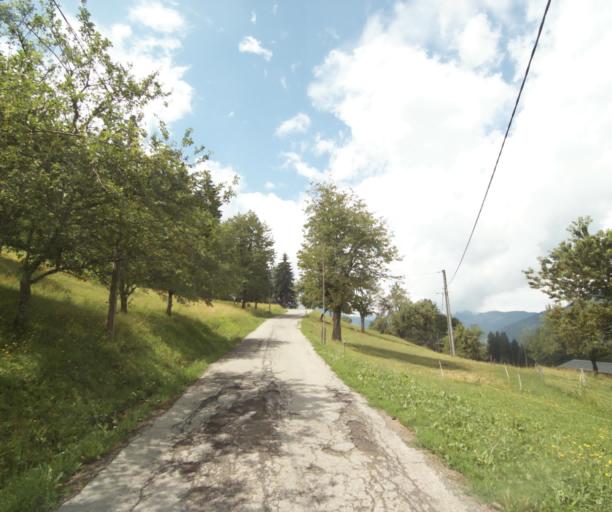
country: FR
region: Rhone-Alpes
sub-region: Departement de la Haute-Savoie
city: Thones
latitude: 45.8960
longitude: 6.3657
